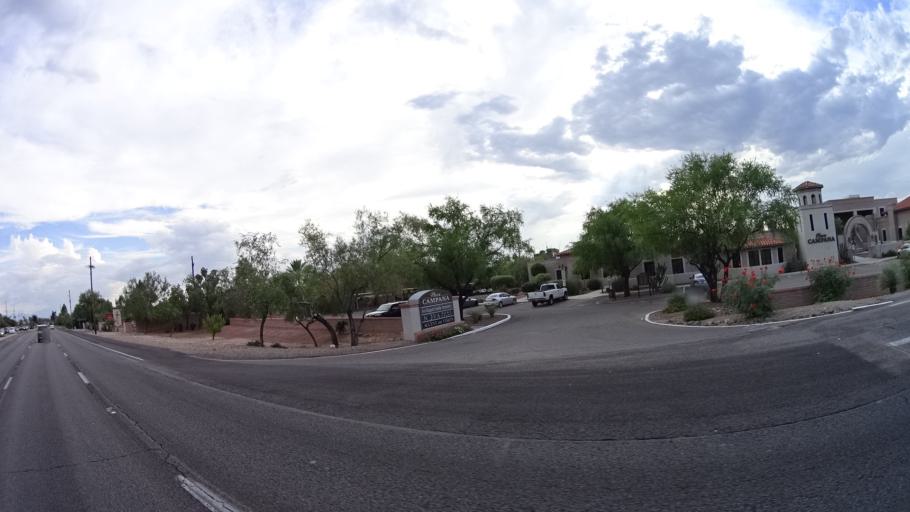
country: US
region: Arizona
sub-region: Pima County
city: Casas Adobes
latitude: 32.3311
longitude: -110.9770
